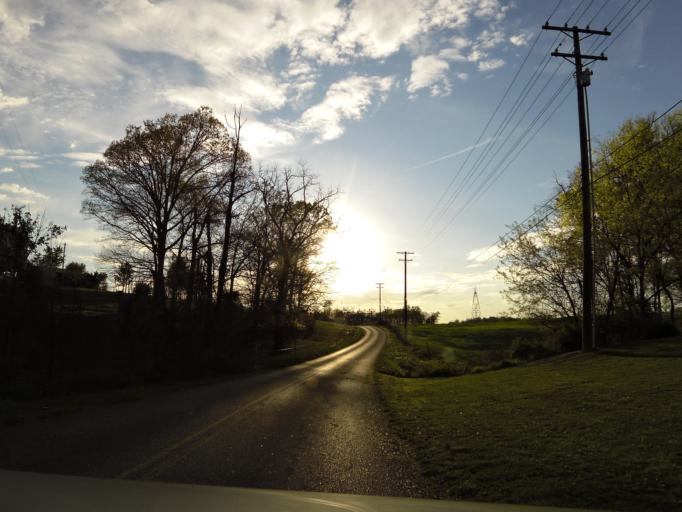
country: US
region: Tennessee
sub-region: Loudon County
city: Greenback
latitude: 35.6302
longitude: -84.0678
